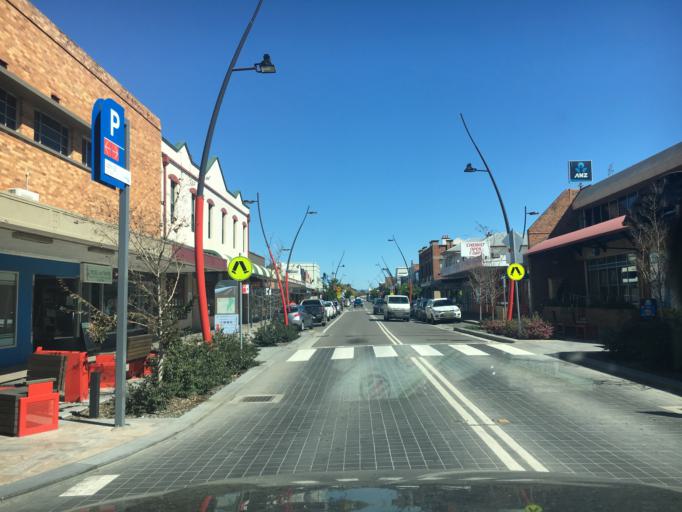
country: AU
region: New South Wales
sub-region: Singleton
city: Singleton
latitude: -32.5648
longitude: 151.1676
